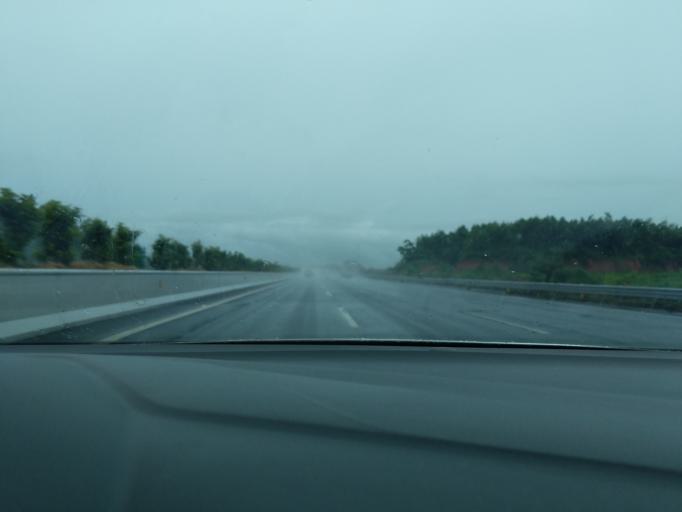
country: CN
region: Guangdong
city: Zhishan
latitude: 22.4855
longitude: 112.7903
